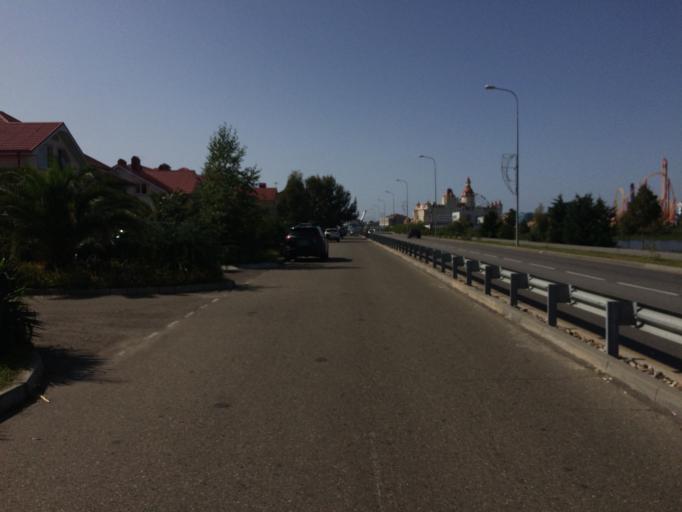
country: RU
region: Krasnodarskiy
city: Adler
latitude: 43.3994
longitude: 39.9720
